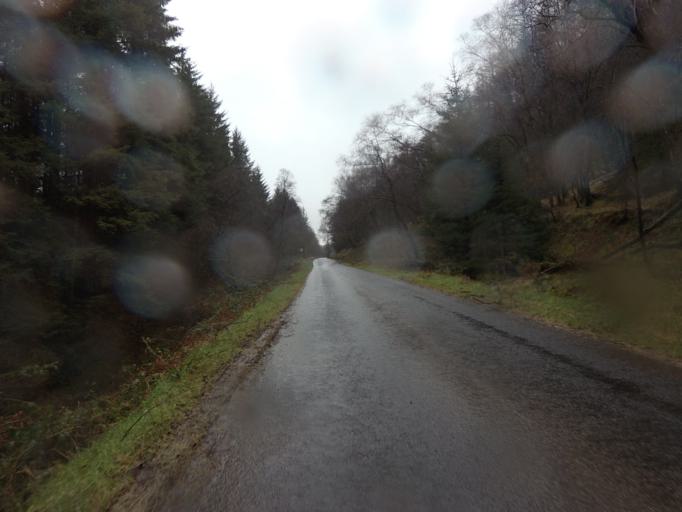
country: GB
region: Scotland
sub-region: West Dunbartonshire
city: Balloch
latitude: 56.2309
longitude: -4.5577
